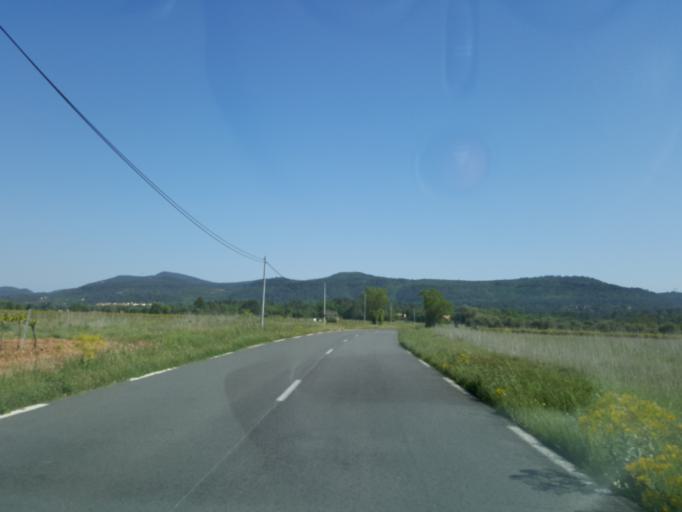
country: FR
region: Provence-Alpes-Cote d'Azur
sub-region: Departement du Var
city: La Roquebrussanne
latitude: 43.3234
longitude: 5.9864
